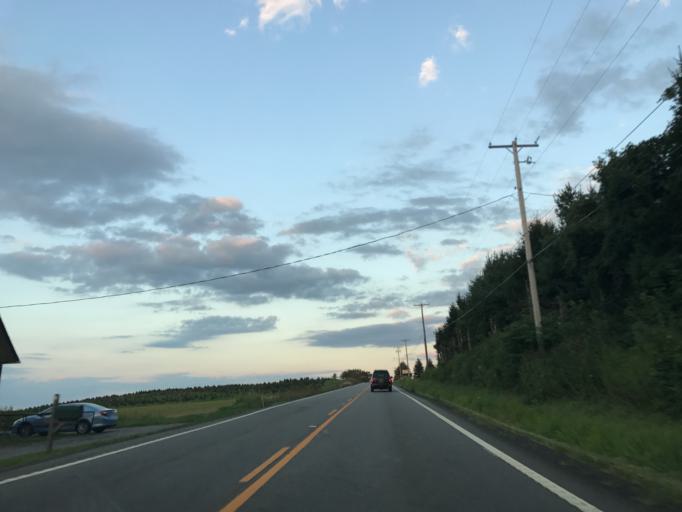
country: US
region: Ohio
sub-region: Columbiana County
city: Lisbon
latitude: 40.7700
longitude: -80.8309
